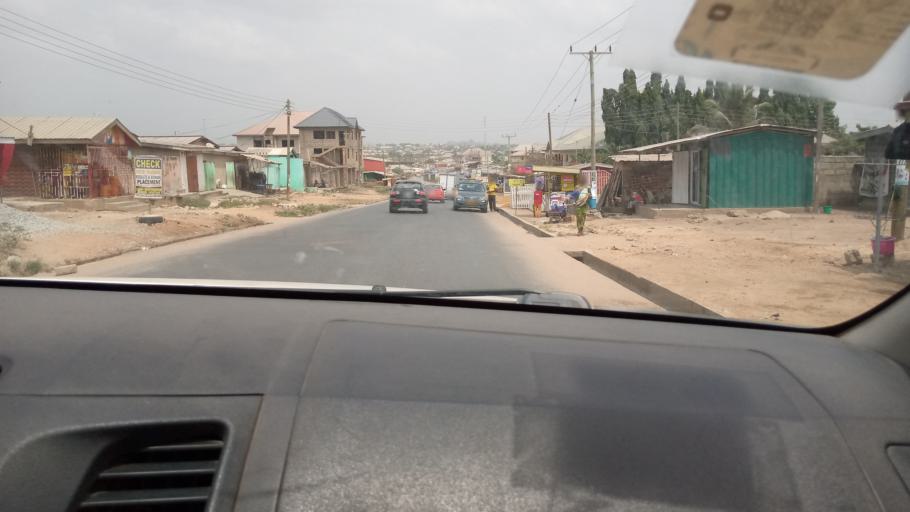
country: GH
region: Central
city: Kasoa
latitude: 5.5316
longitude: -0.4509
